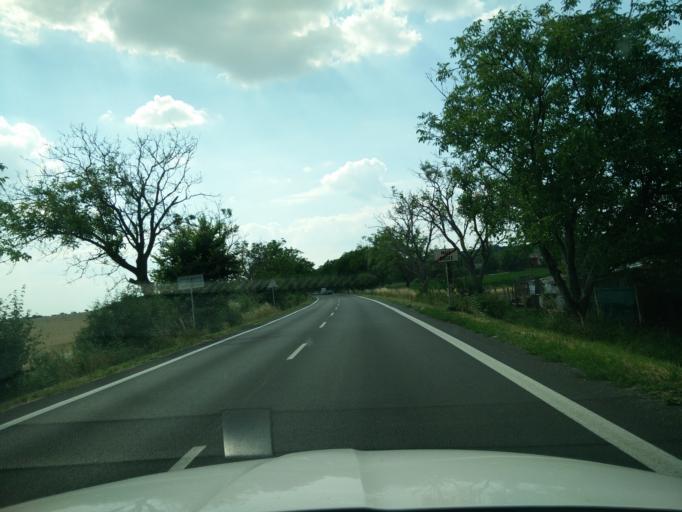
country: SK
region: Nitriansky
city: Partizanske
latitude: 48.6307
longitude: 18.3305
